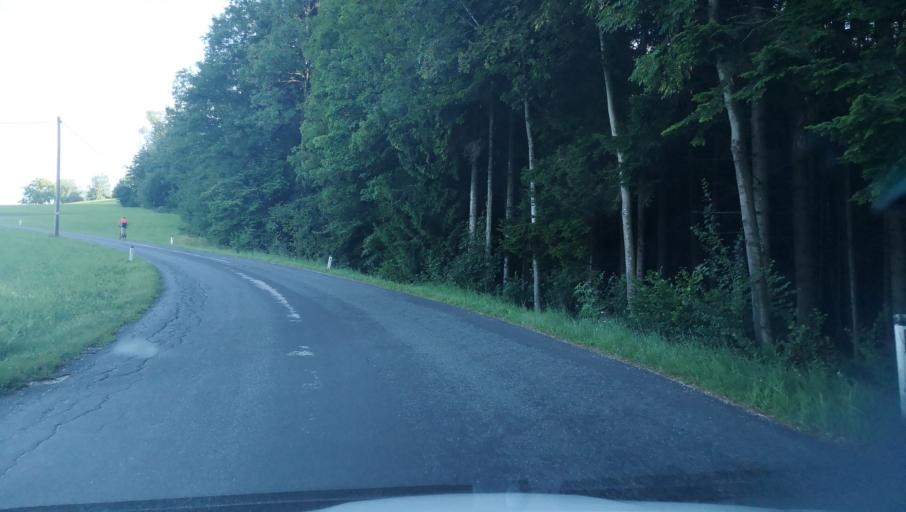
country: AT
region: Lower Austria
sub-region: Politischer Bezirk Amstetten
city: Neuhofen an der Ybbs
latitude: 47.9991
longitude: 14.8723
